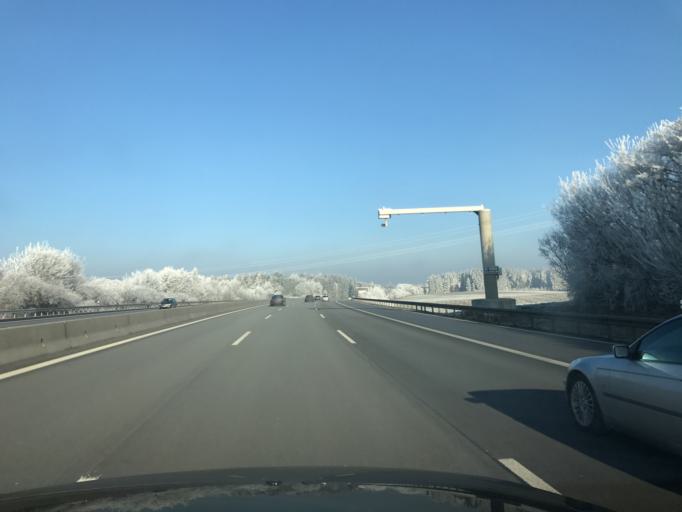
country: DE
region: Bavaria
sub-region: Upper Bavaria
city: Paunzhausen
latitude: 48.4740
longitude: 11.5853
